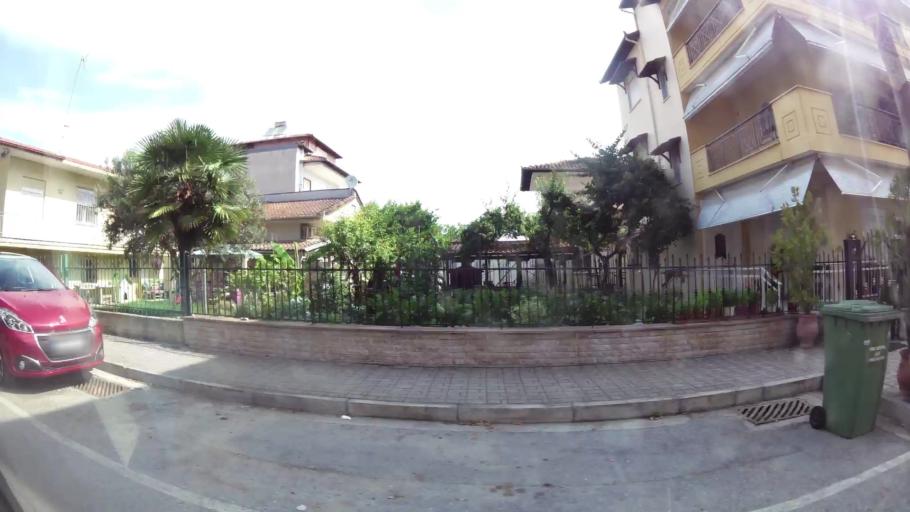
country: GR
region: Central Macedonia
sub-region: Nomos Pierias
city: Katerini
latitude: 40.2760
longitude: 22.5152
